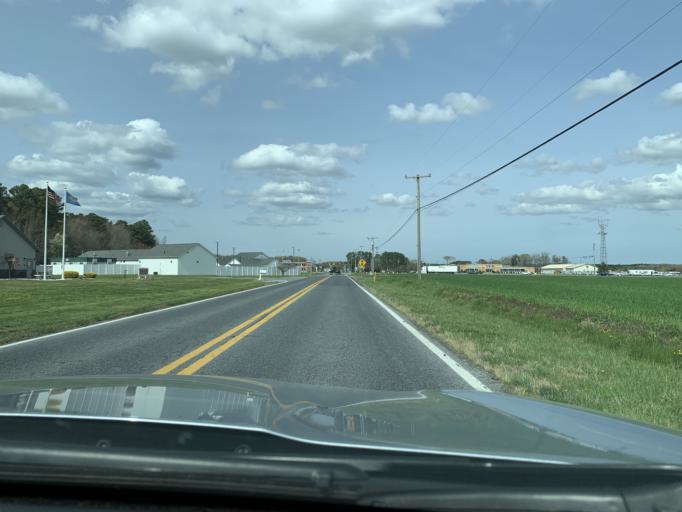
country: US
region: Delaware
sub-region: Sussex County
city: Georgetown
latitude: 38.6615
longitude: -75.3795
